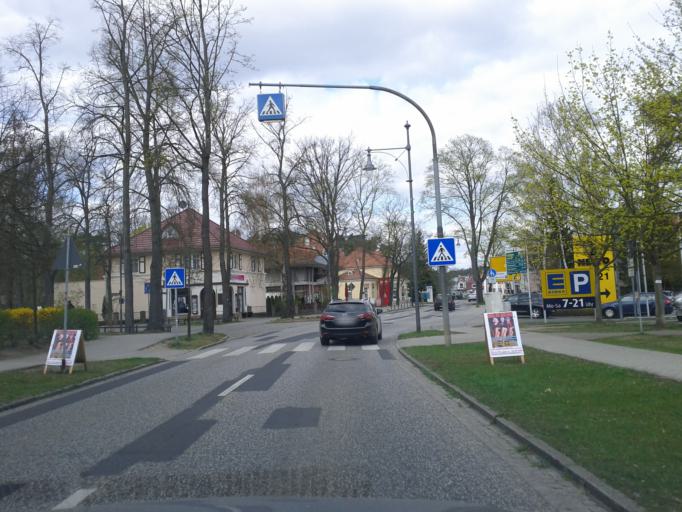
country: DE
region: Brandenburg
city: Bad Saarow
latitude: 52.2916
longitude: 14.0635
